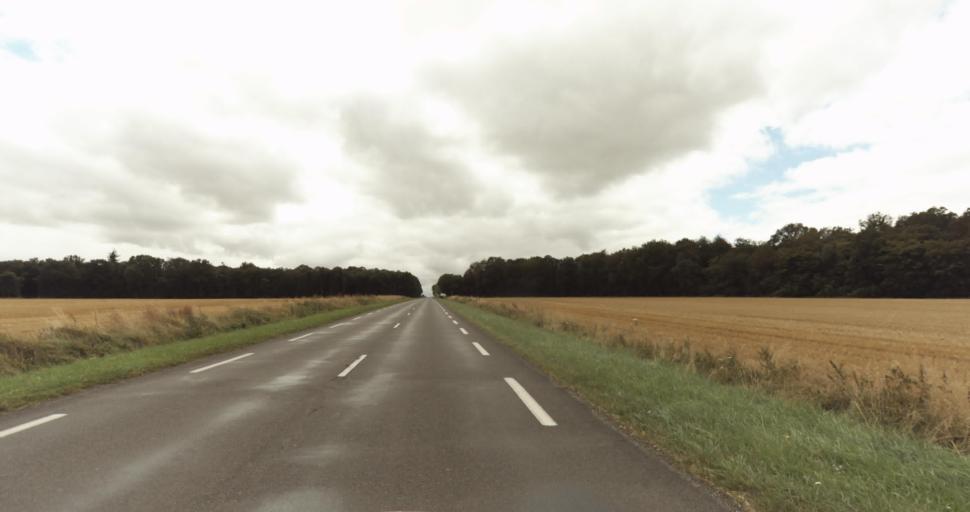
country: FR
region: Haute-Normandie
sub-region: Departement de l'Eure
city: Evreux
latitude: 48.9654
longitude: 1.1603
